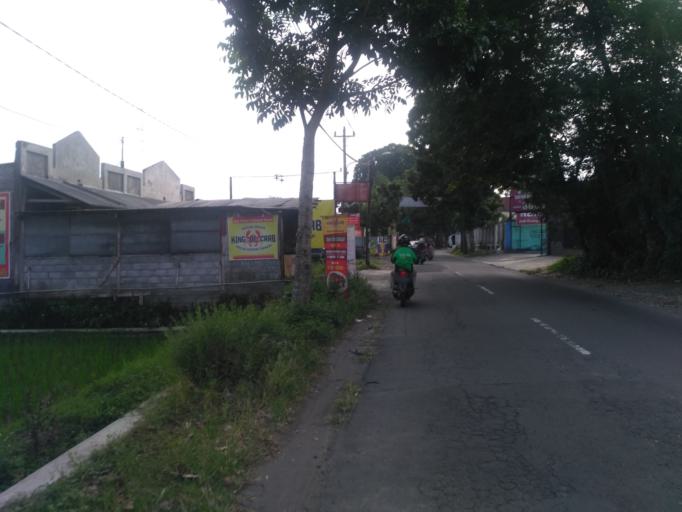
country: ID
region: Daerah Istimewa Yogyakarta
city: Yogyakarta
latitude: -7.7631
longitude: 110.3450
